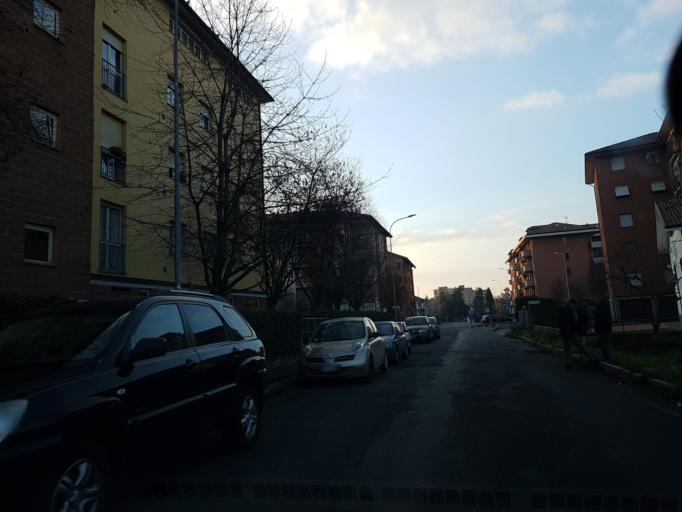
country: IT
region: Piedmont
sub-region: Provincia di Alessandria
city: Novi Ligure
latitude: 44.7583
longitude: 8.8043
